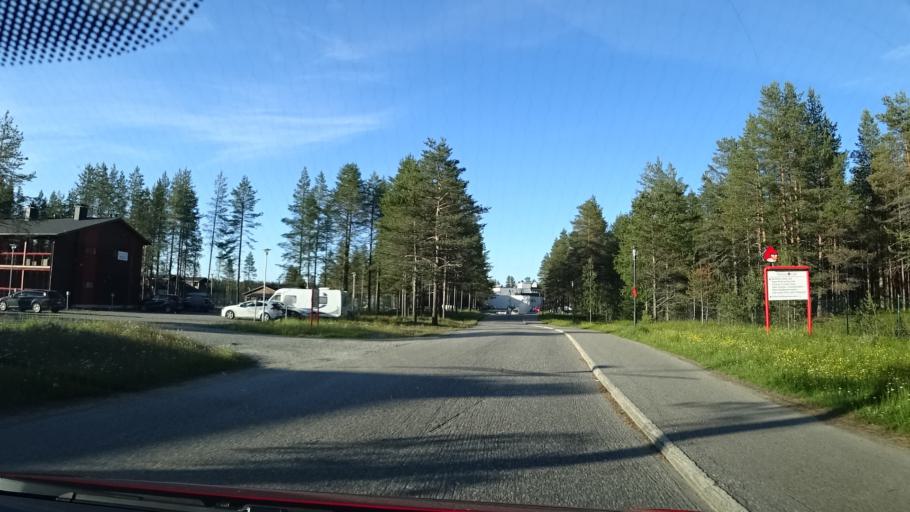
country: FI
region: Northern Ostrobothnia
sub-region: Koillismaa
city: Kuusamo
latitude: 66.0000
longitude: 29.1617
